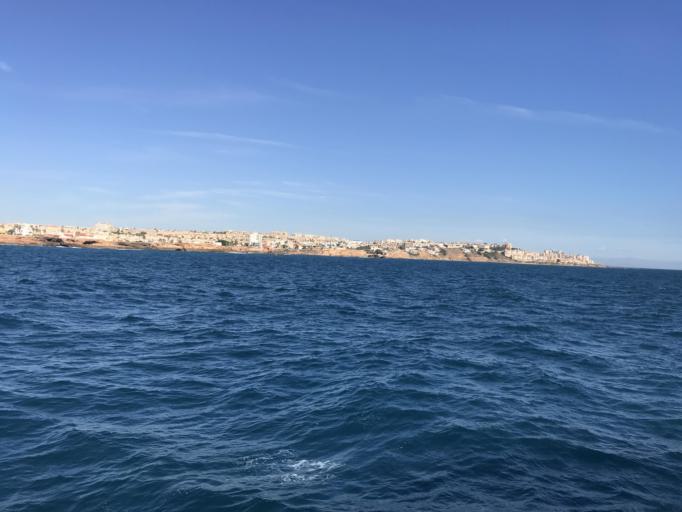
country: ES
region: Valencia
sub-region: Provincia de Alicante
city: Torrevieja
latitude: 37.9843
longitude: -0.6509
